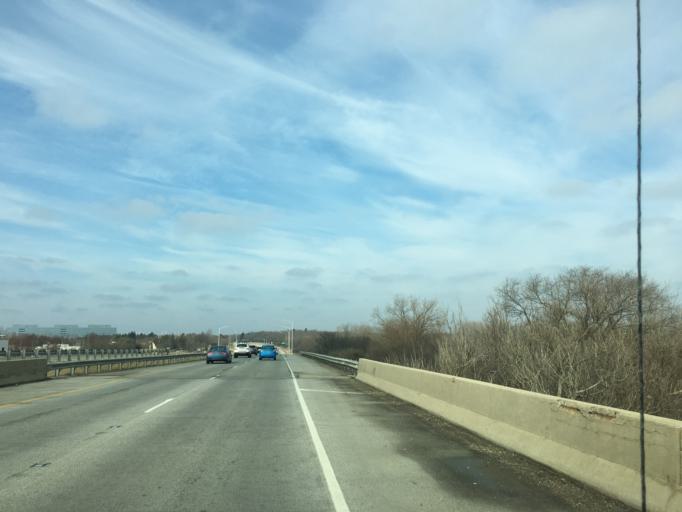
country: US
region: Illinois
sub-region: Cook County
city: Streamwood
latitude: 42.0777
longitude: -88.2007
